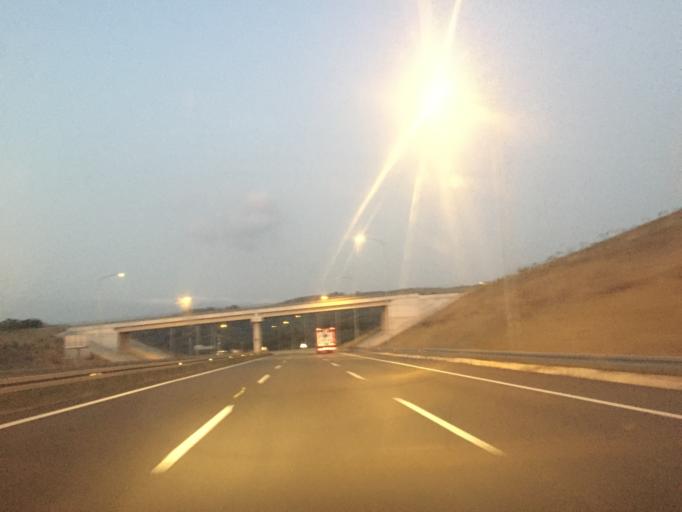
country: TR
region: Bursa
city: Demirtas
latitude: 40.3316
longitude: 29.1107
